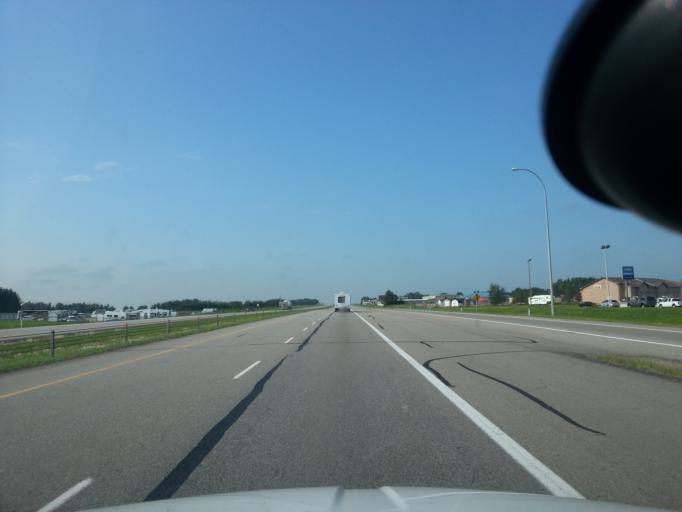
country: CA
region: Alberta
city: Penhold
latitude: 52.0247
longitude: -113.9330
